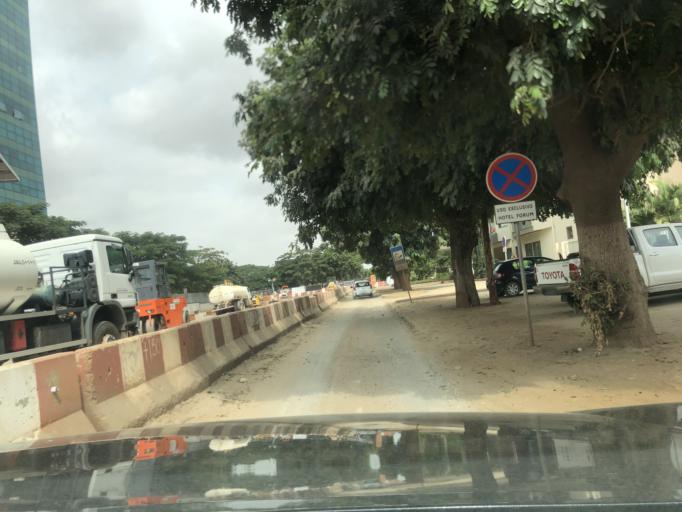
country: AO
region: Luanda
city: Luanda
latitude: -8.8373
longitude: 13.2345
